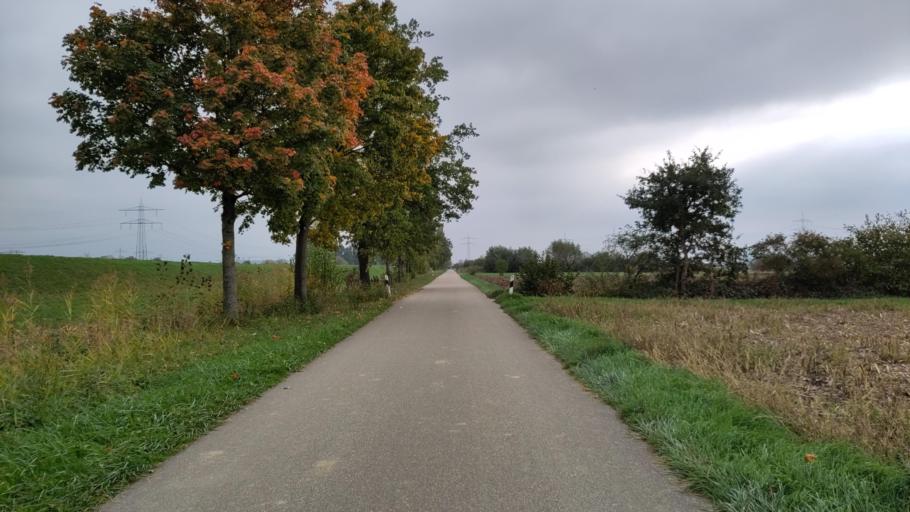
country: DE
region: Baden-Wuerttemberg
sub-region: Freiburg Region
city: Riegel
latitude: 48.1391
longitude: 7.7559
